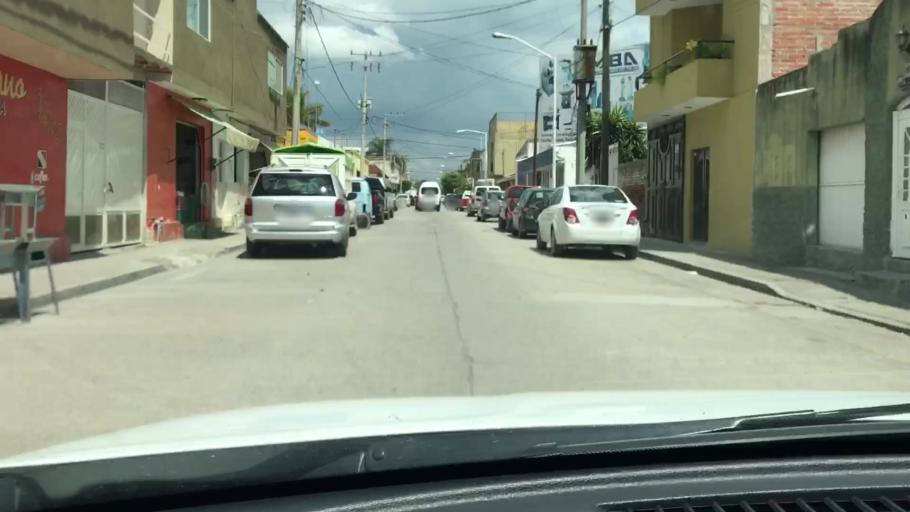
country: MX
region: Guanajuato
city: San Francisco del Rincon
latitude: 21.0306
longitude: -101.8604
